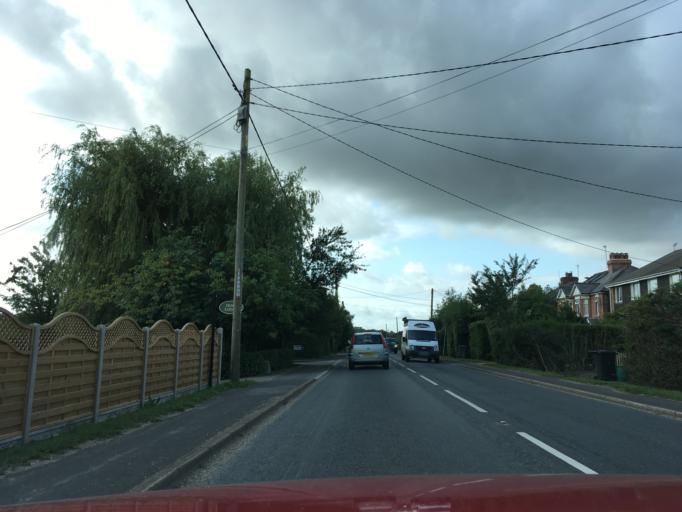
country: GB
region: England
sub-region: Hampshire
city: Bishops Waltham
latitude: 50.9347
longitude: -1.2009
